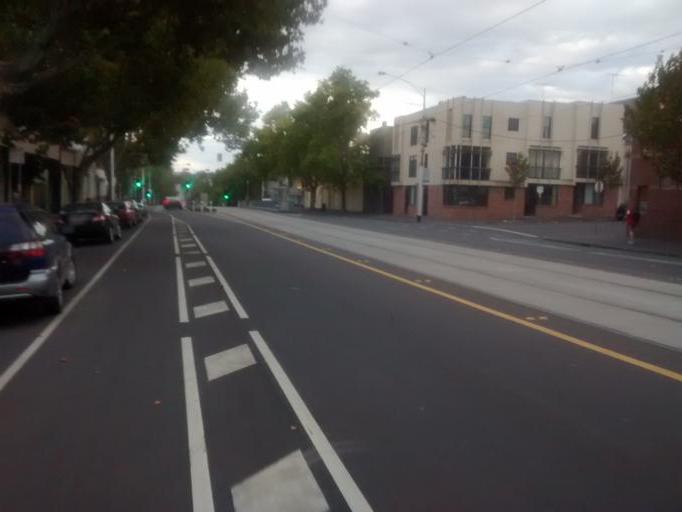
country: AU
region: Victoria
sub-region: Melbourne
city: North Melbourne
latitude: -37.8017
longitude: 144.9456
